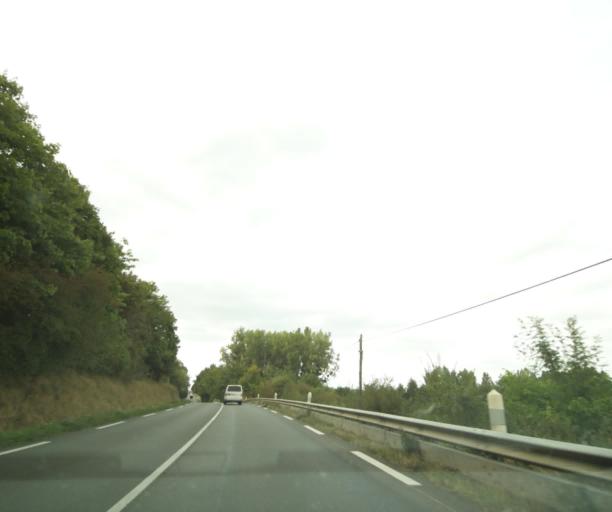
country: FR
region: Centre
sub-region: Departement d'Indre-et-Loire
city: Loches
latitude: 47.1545
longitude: 0.9971
